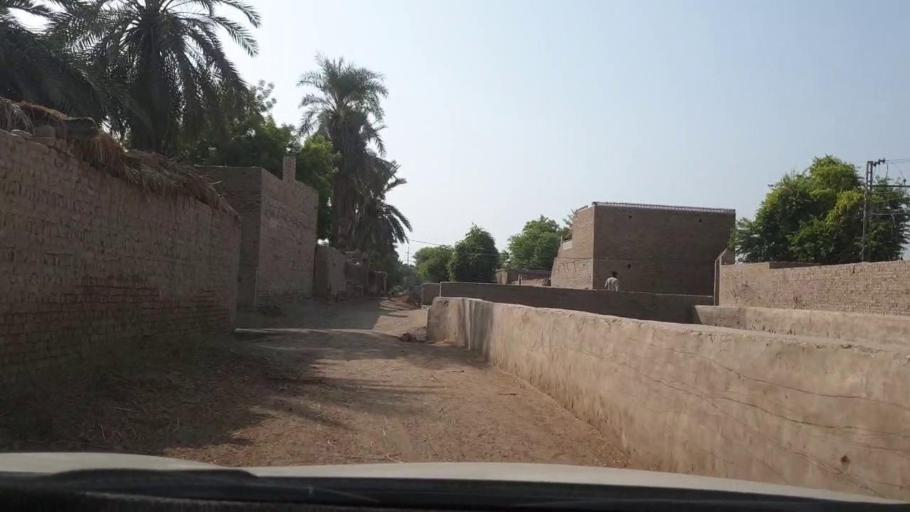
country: PK
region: Sindh
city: Larkana
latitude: 27.4637
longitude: 68.2444
